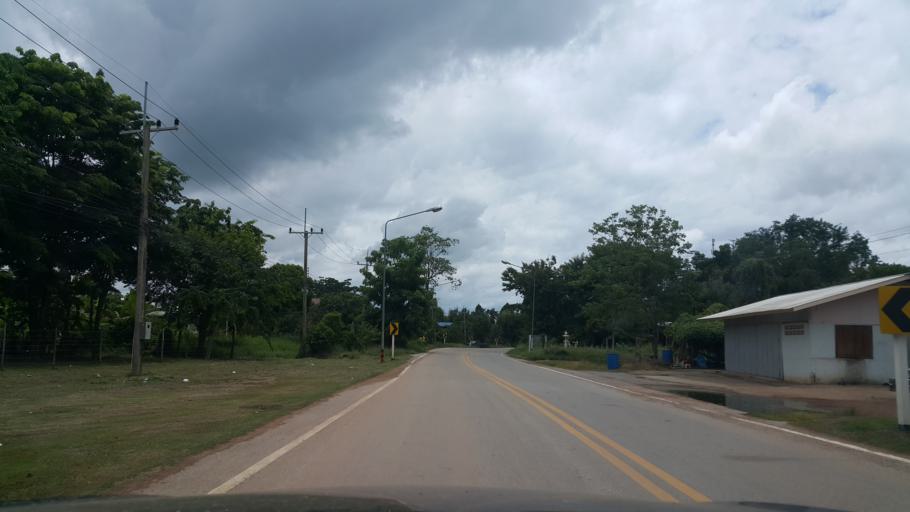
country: TH
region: Sukhothai
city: Kong Krailat
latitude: 16.9072
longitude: 99.8803
